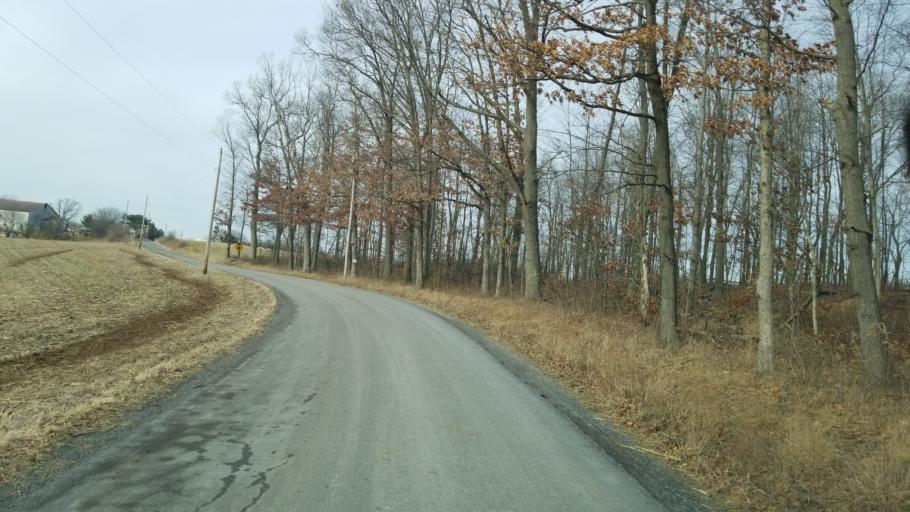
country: US
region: Pennsylvania
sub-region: Jefferson County
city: Punxsutawney
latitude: 40.8799
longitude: -79.0628
